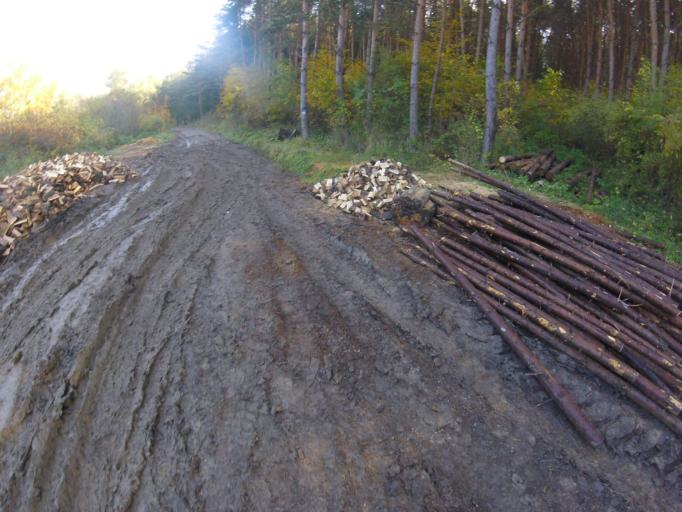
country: HU
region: Borsod-Abauj-Zemplen
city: Putnok
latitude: 48.2192
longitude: 20.4410
